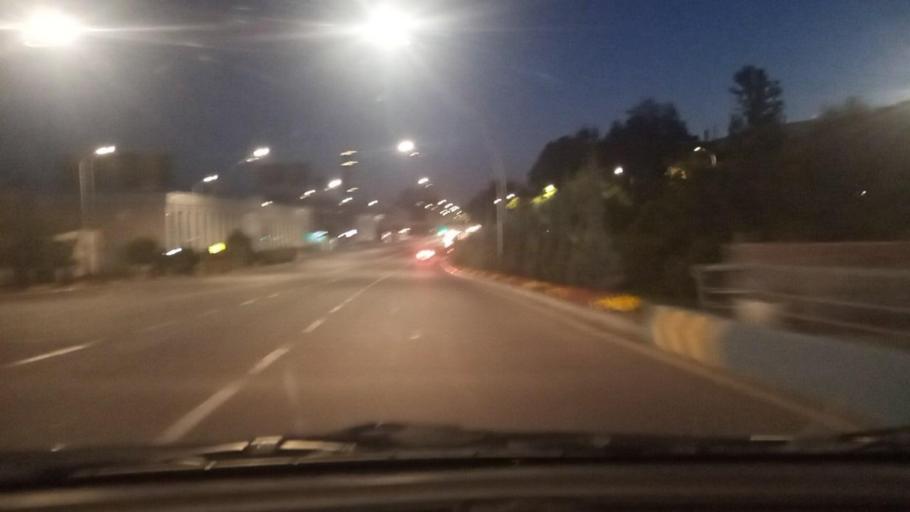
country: UZ
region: Toshkent Shahri
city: Tashkent
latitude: 41.2697
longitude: 69.2609
